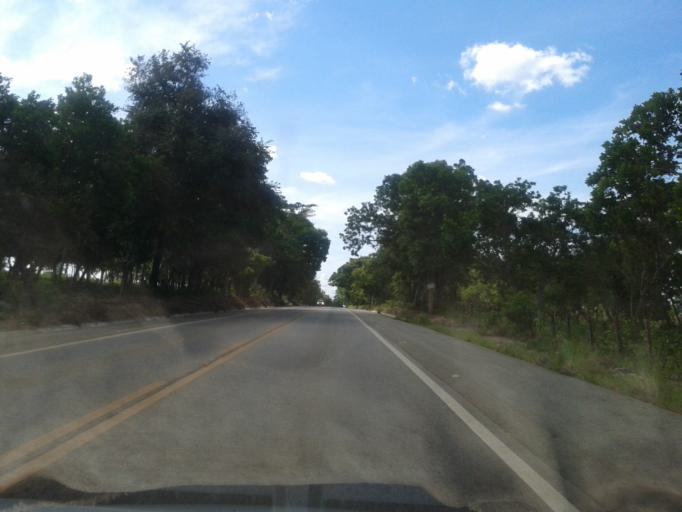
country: BR
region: Goias
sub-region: Itapuranga
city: Itapuranga
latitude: -15.4680
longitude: -50.3488
